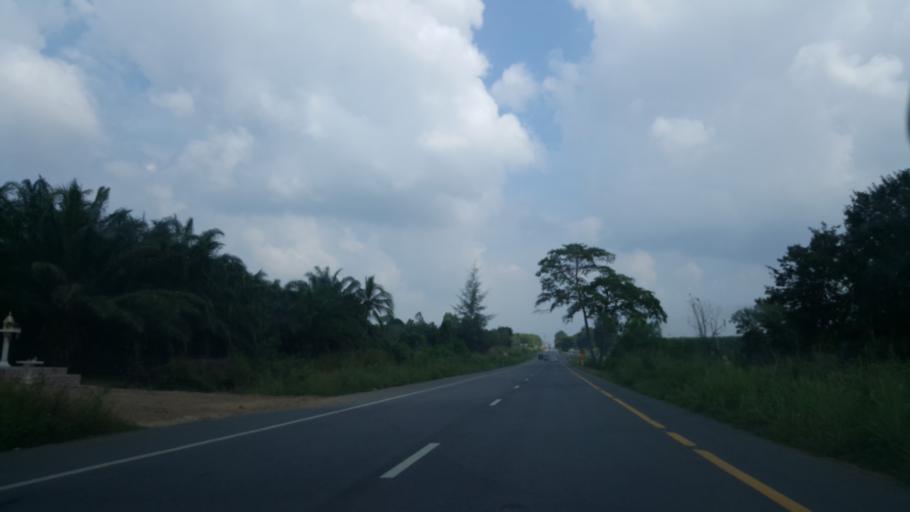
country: TH
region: Rayong
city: Ban Chang
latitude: 12.7673
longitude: 100.9916
